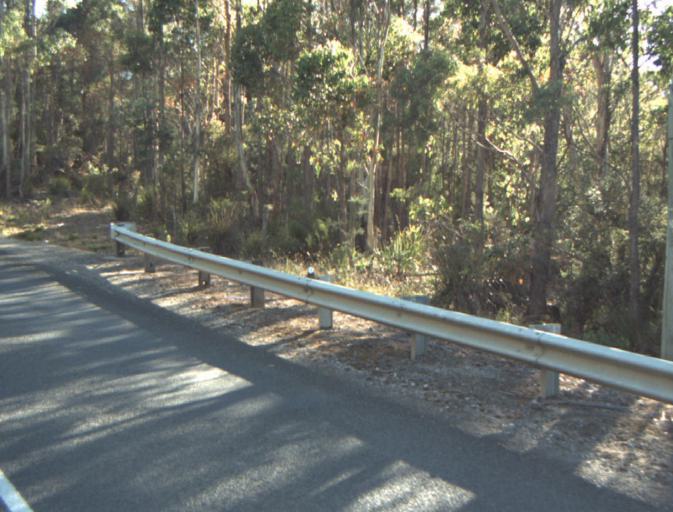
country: AU
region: Tasmania
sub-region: Launceston
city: Mayfield
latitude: -41.3242
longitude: 147.1868
